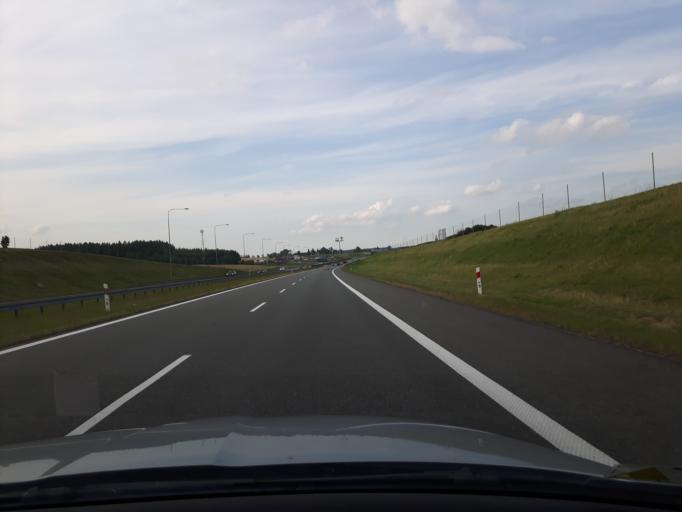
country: PL
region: Warmian-Masurian Voivodeship
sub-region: Powiat ostrodzki
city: Maldyty
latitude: 53.8759
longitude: 19.7377
